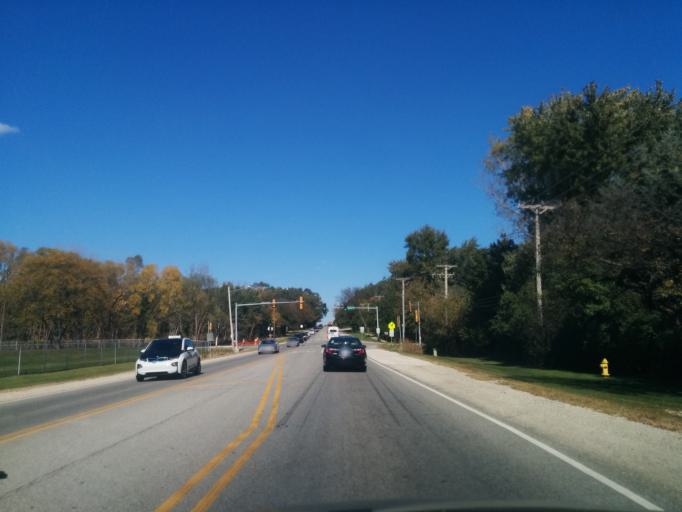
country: US
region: Illinois
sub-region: DuPage County
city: Glen Ellyn
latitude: 41.8515
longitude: -88.0528
